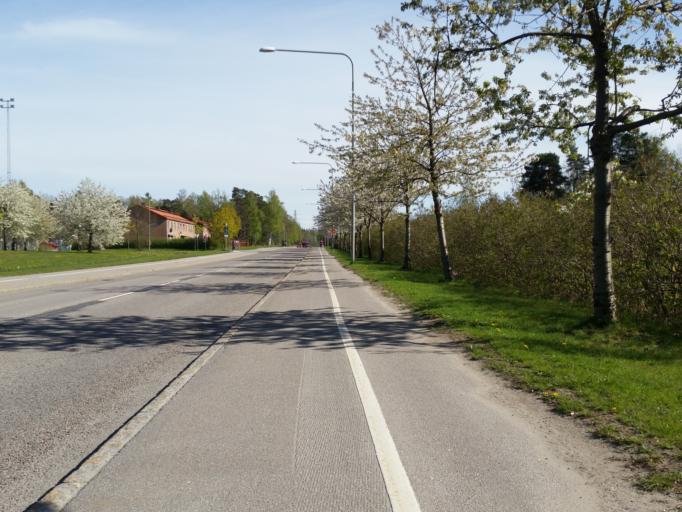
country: SE
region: Stockholm
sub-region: Nacka Kommun
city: Nacka
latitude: 59.2680
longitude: 18.1168
